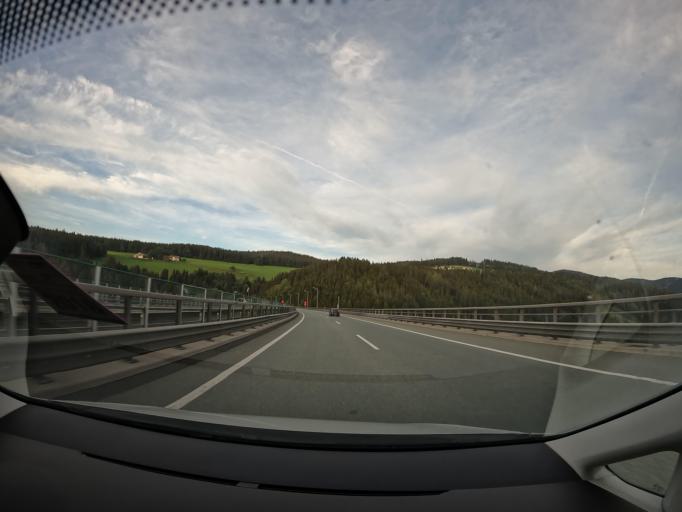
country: AT
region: Styria
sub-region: Politischer Bezirk Voitsberg
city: Pack
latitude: 46.9214
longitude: 14.9952
